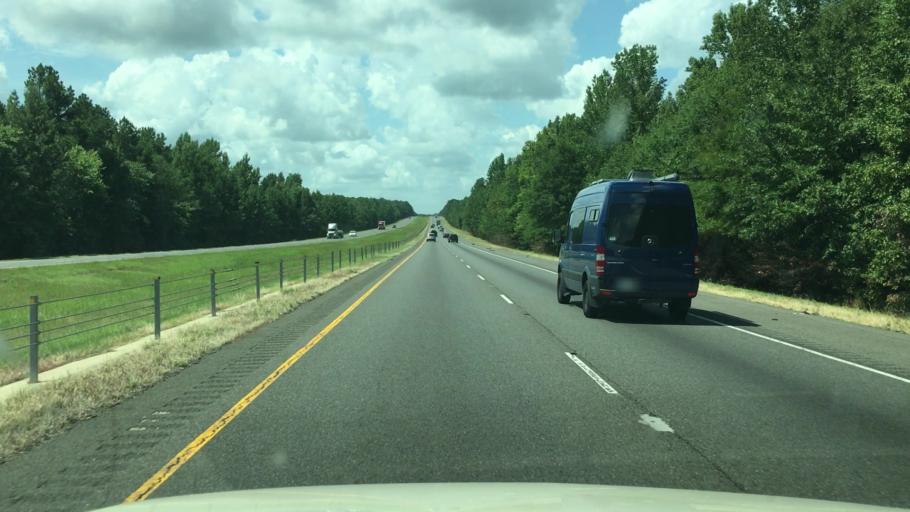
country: US
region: Arkansas
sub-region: Clark County
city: Arkadelphia
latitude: 34.0557
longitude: -93.1312
